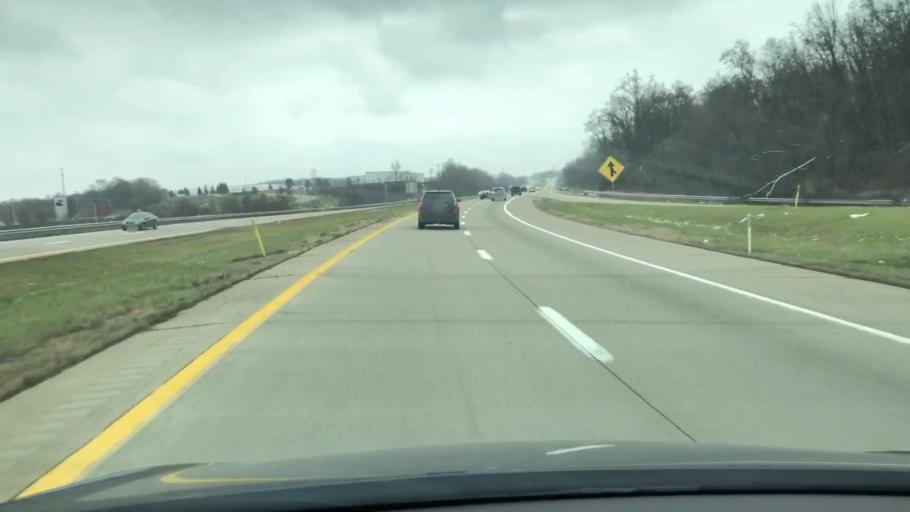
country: US
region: Pennsylvania
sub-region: Westmoreland County
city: New Stanton
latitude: 40.1945
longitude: -79.5719
